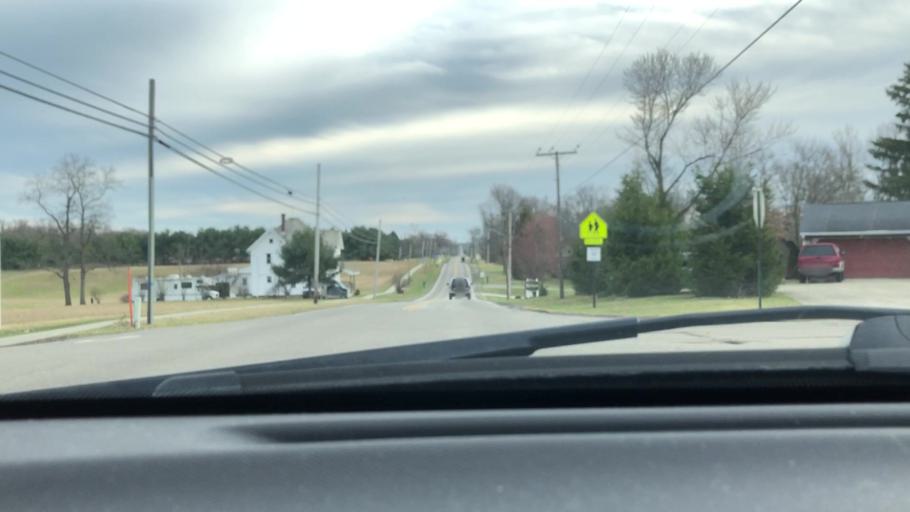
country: US
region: Ohio
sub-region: Wayne County
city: Dalton
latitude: 40.7559
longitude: -81.7452
